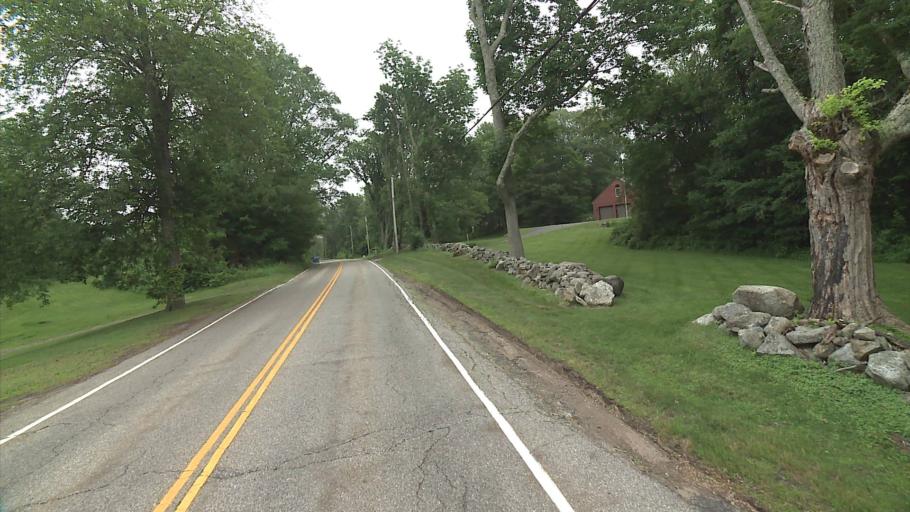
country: US
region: Connecticut
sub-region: Tolland County
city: Hebron
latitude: 41.7078
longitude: -72.3670
